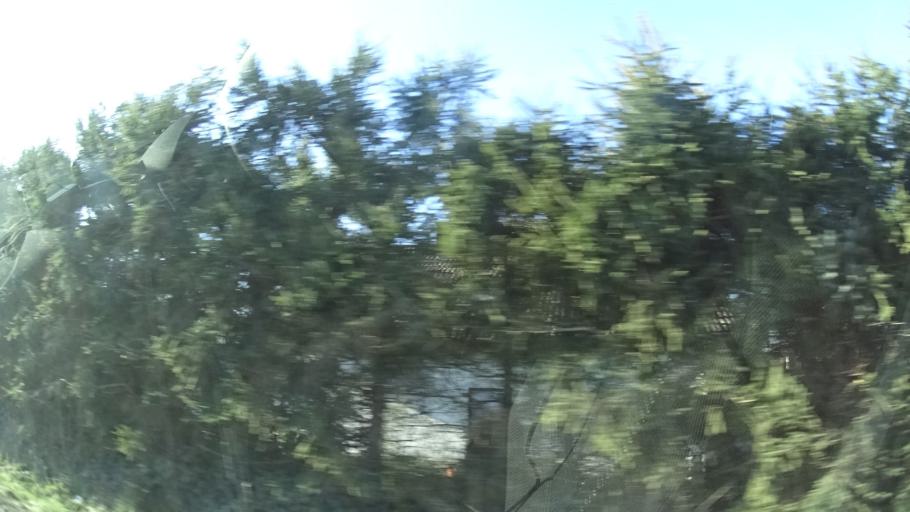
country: DE
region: Hesse
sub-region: Regierungsbezirk Darmstadt
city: Schluchtern
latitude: 50.3522
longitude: 9.5371
